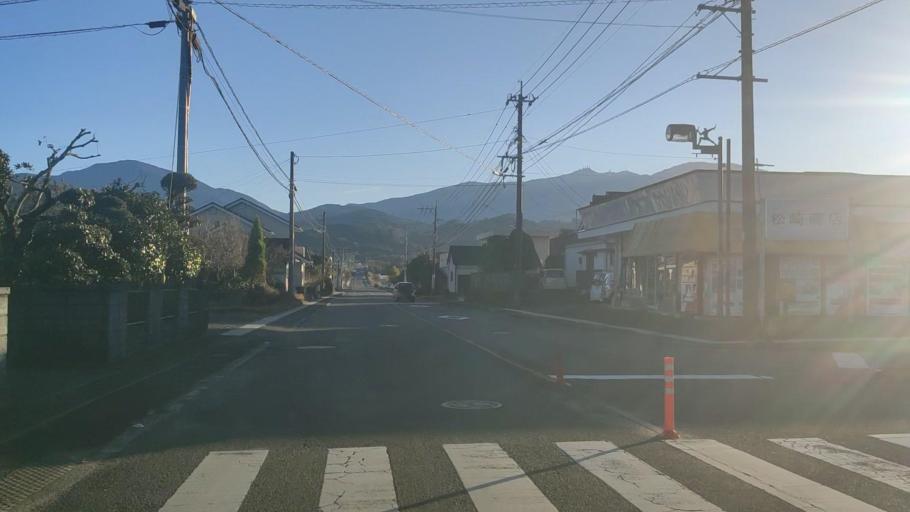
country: JP
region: Miyazaki
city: Miyazaki-shi
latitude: 31.8310
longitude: 131.2991
